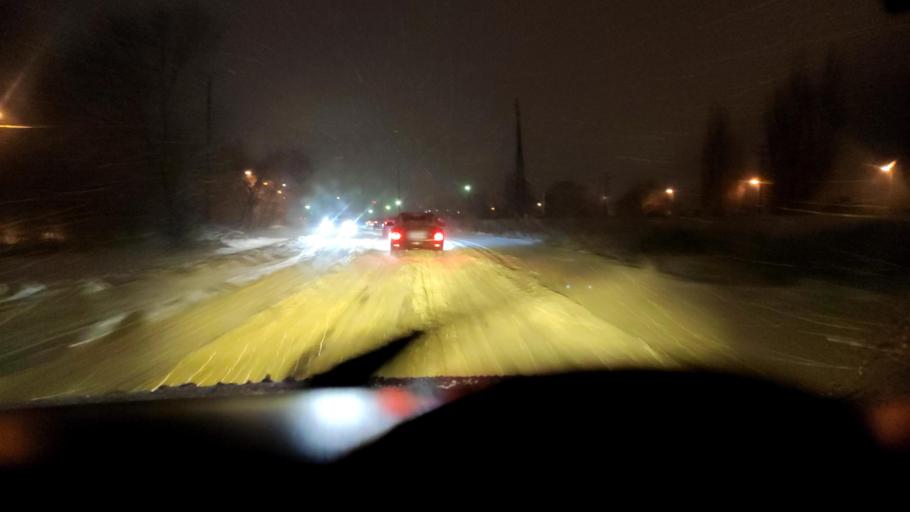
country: RU
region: Voronezj
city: Pridonskoy
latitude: 51.6806
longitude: 39.0720
